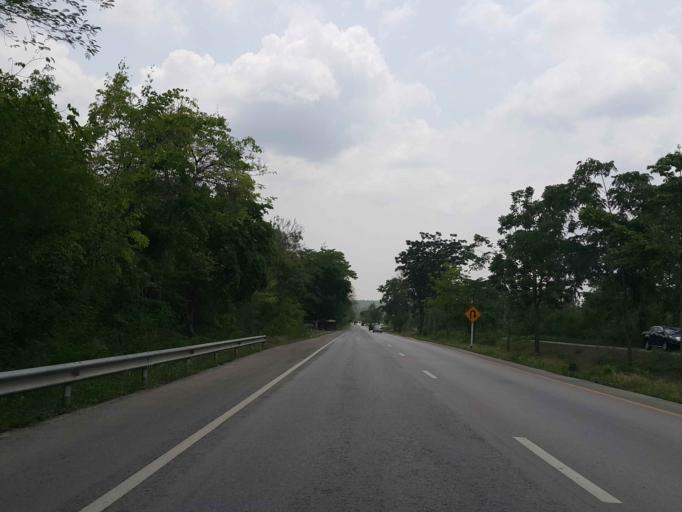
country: TH
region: Lampang
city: Ko Kha
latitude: 18.0776
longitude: 99.3935
